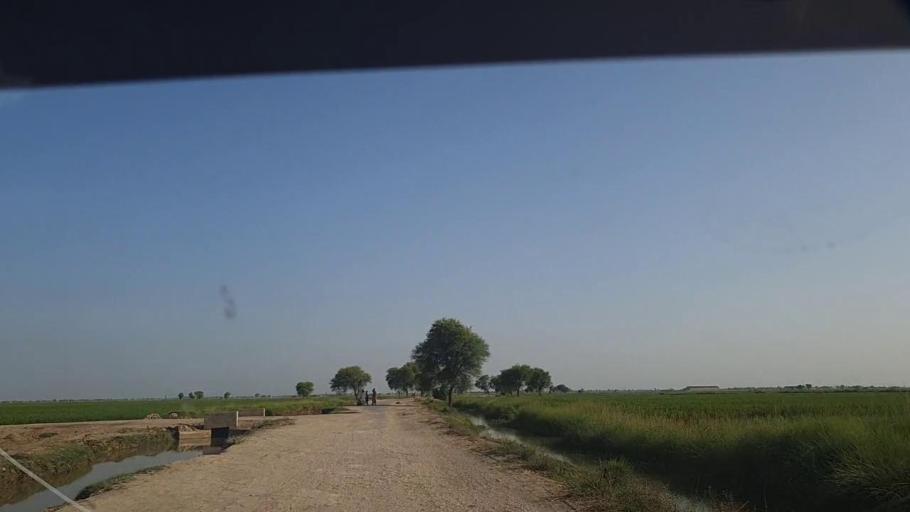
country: PK
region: Sindh
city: Tangwani
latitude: 28.2618
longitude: 69.0134
